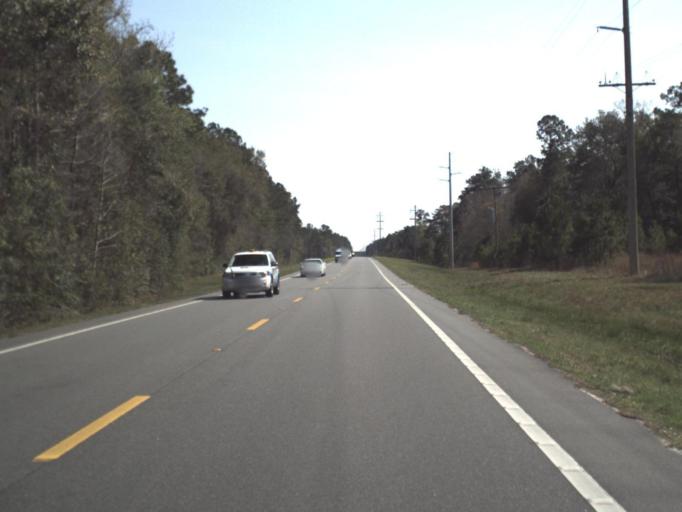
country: US
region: Florida
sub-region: Franklin County
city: Carrabelle
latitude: 29.9930
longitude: -84.5033
